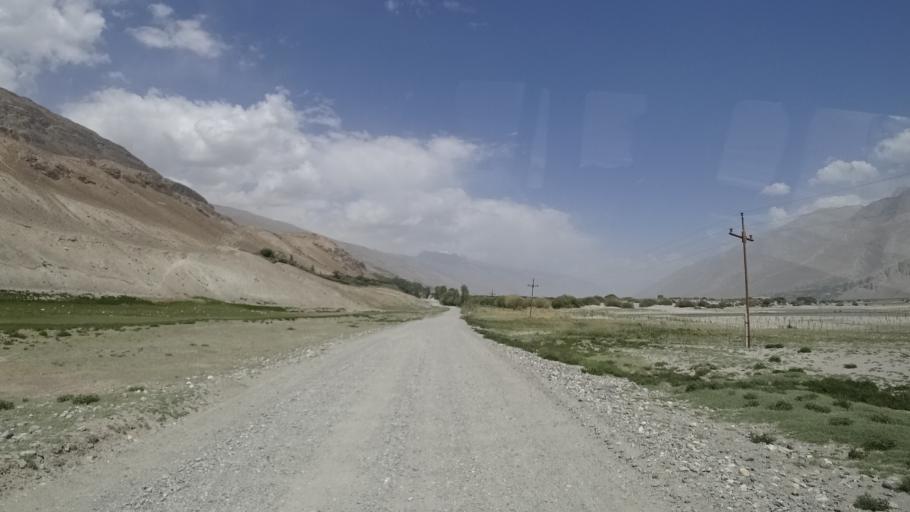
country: AF
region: Badakhshan
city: Khandud
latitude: 36.9319
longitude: 72.2099
